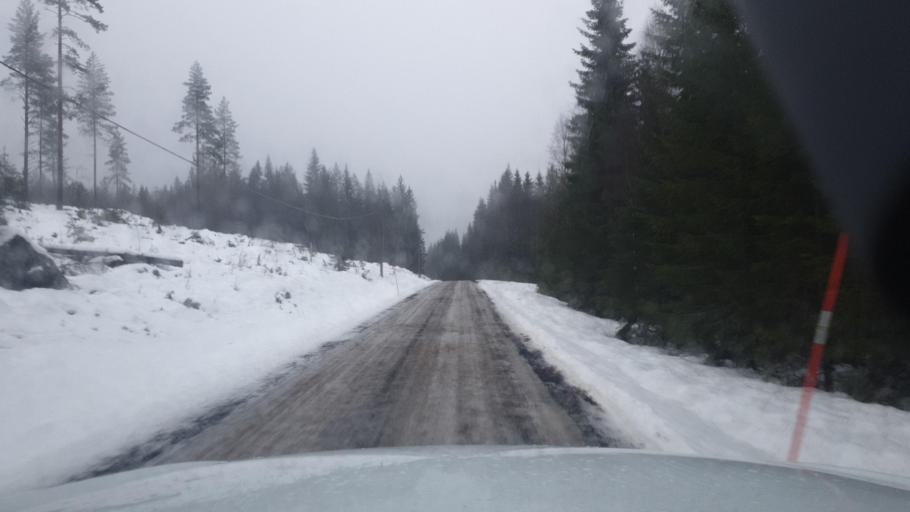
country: SE
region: Vaermland
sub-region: Eda Kommun
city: Charlottenberg
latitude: 60.1321
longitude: 12.5920
